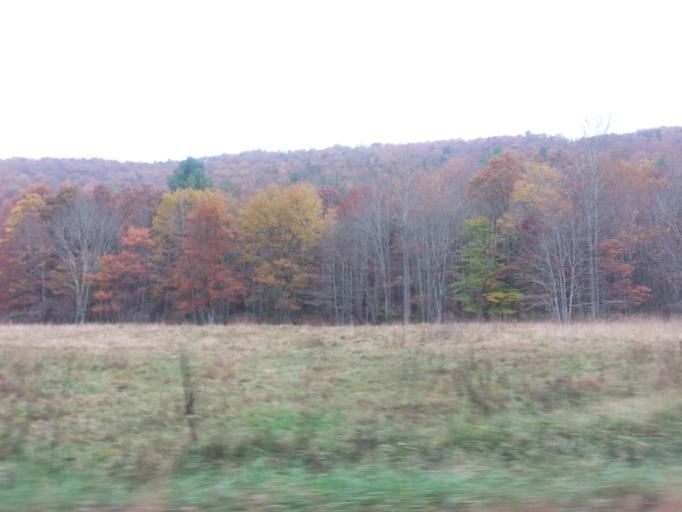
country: US
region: Virginia
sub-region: Bland County
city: Bland
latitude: 37.0607
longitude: -81.0199
